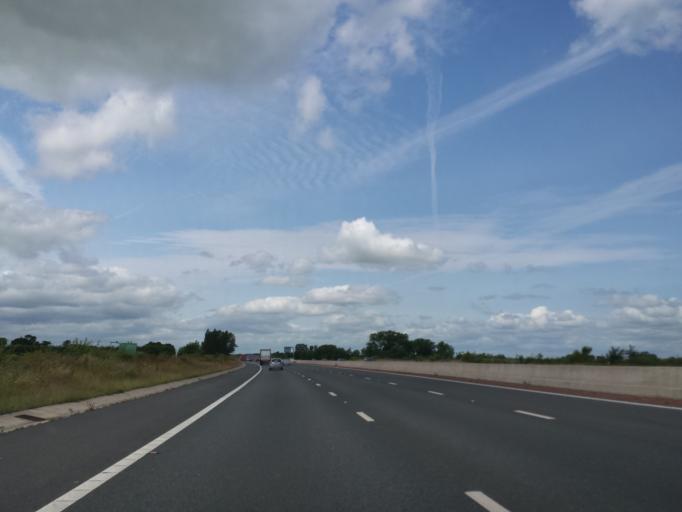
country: GB
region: England
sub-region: North Yorkshire
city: Bedale
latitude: 54.2448
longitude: -1.5024
